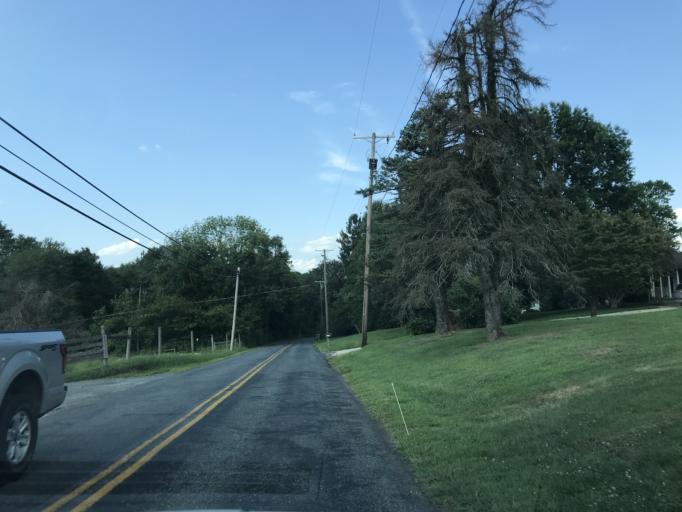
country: US
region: Maryland
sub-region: Harford County
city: South Bel Air
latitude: 39.6086
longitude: -76.2990
